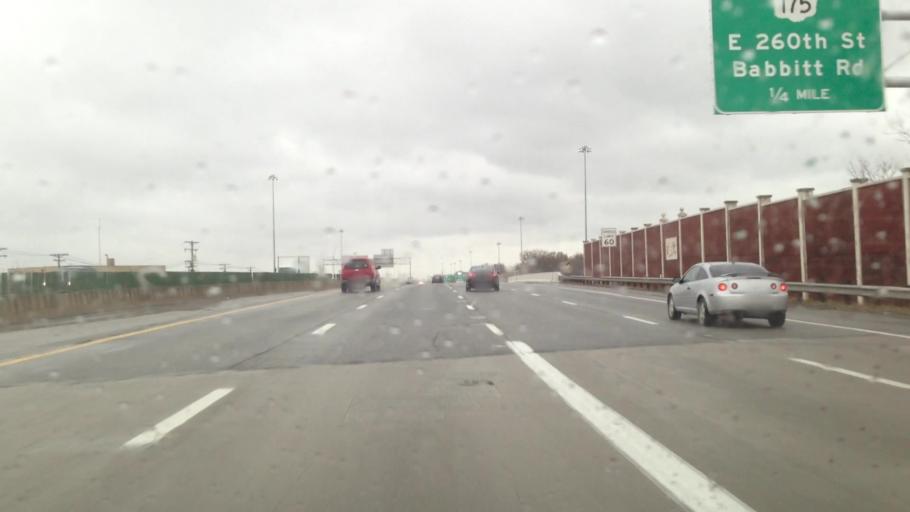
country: US
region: Ohio
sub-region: Cuyahoga County
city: Euclid
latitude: 41.6023
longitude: -81.5016
